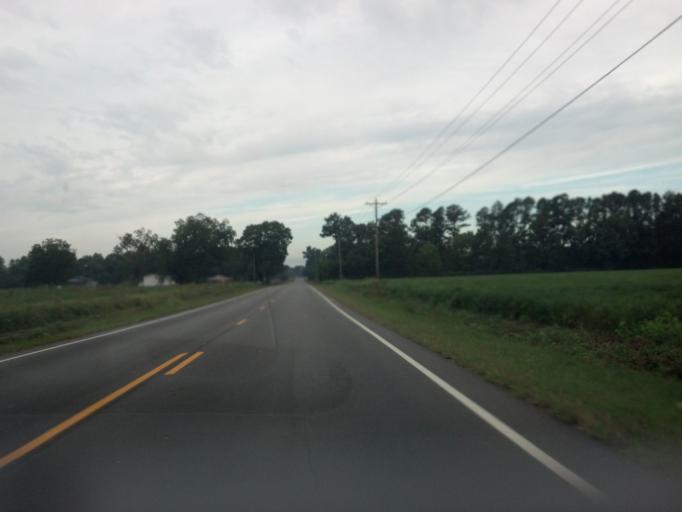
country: US
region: North Carolina
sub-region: Greene County
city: Maury
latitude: 35.4695
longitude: -77.5292
